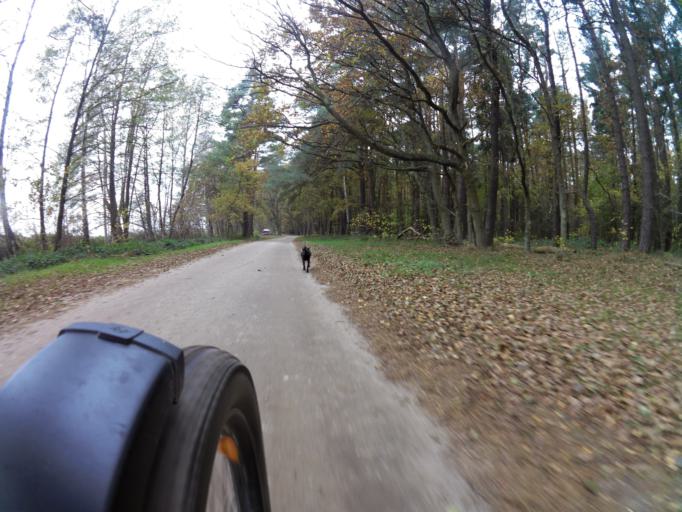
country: PL
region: Pomeranian Voivodeship
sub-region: Powiat pucki
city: Krokowa
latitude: 54.8289
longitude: 18.1278
